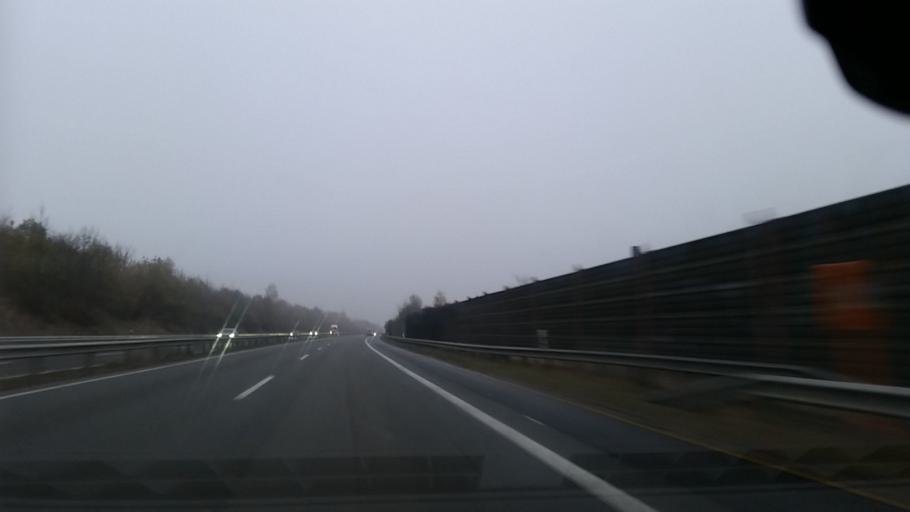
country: DE
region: Lower Saxony
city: Bardowick
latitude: 53.2881
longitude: 10.3787
